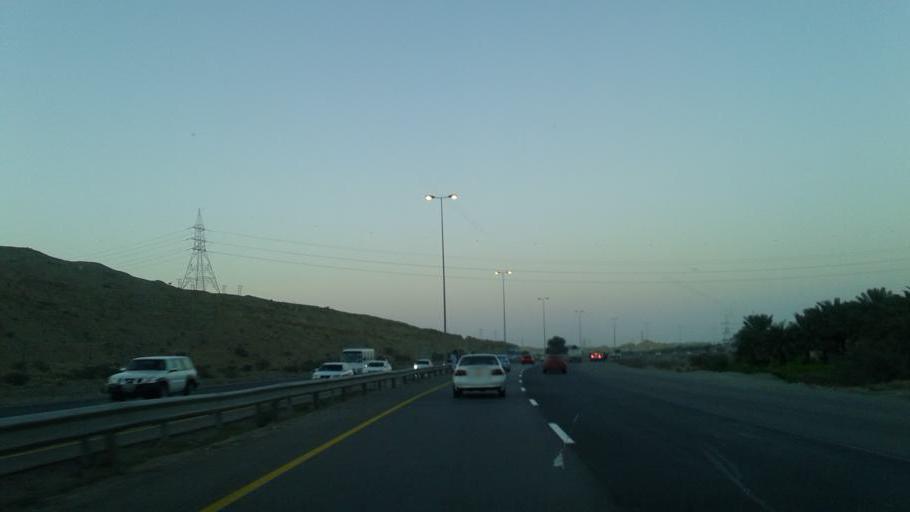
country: OM
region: Muhafazat Masqat
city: As Sib al Jadidah
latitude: 23.5415
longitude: 58.1886
